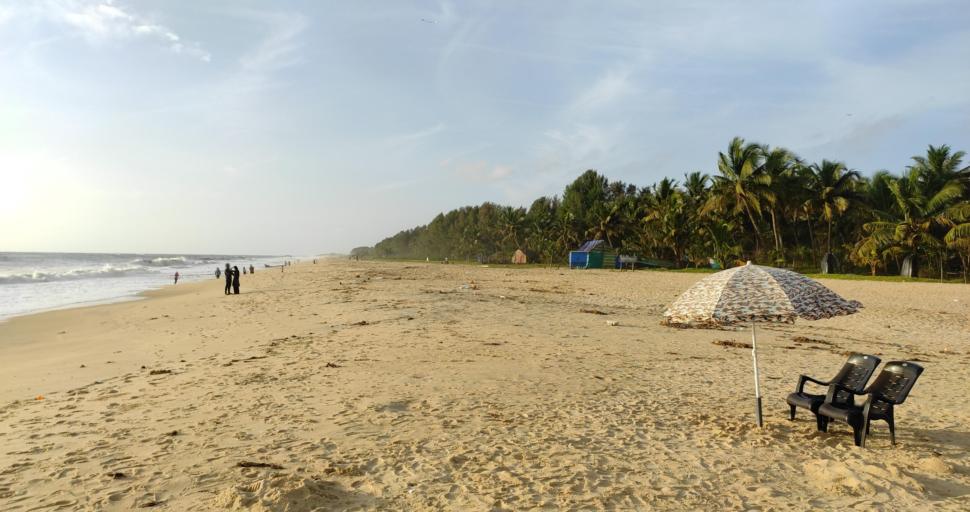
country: IN
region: Kerala
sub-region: Alappuzha
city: Shertallai
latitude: 9.6017
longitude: 76.2981
